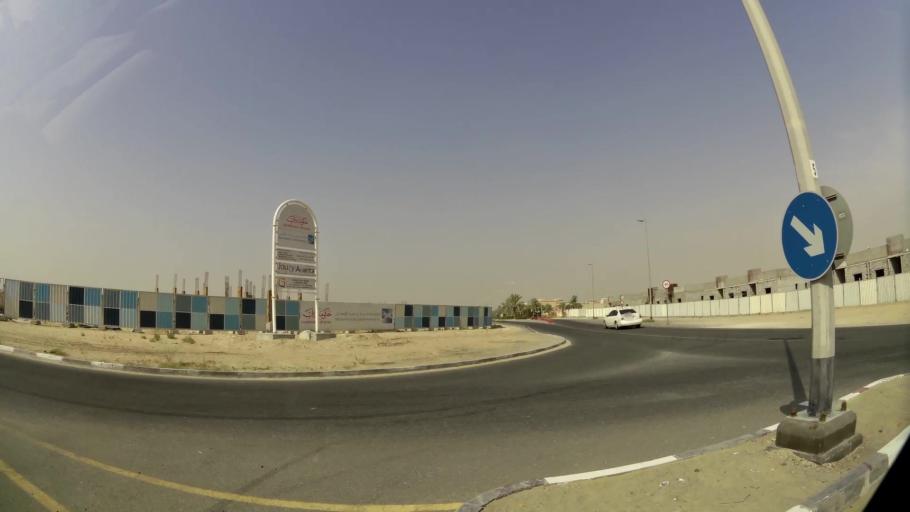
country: AE
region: Ash Shariqah
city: Sharjah
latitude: 25.2628
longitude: 55.4426
